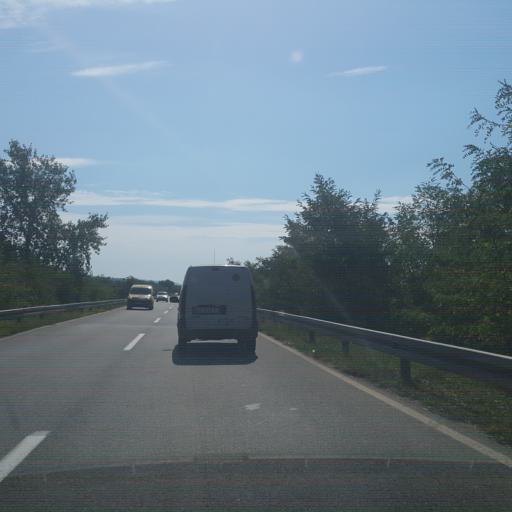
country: RS
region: Central Serbia
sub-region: Zajecarski Okrug
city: Knjazevac
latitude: 43.6441
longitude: 22.2812
